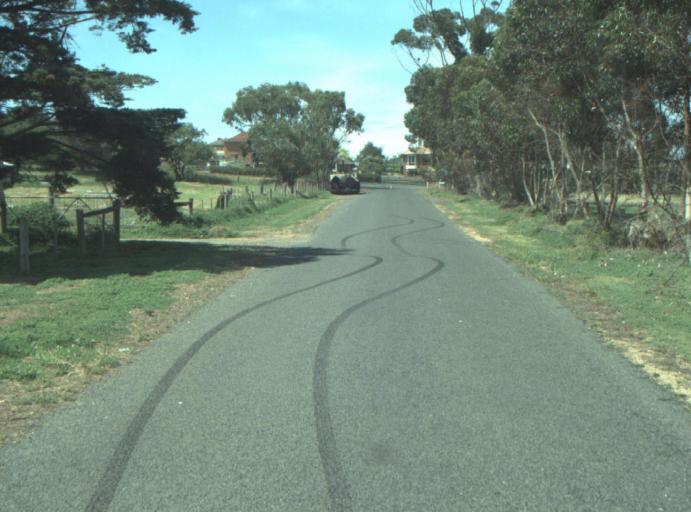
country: AU
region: Victoria
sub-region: Greater Geelong
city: Leopold
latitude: -38.1745
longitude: 144.4712
